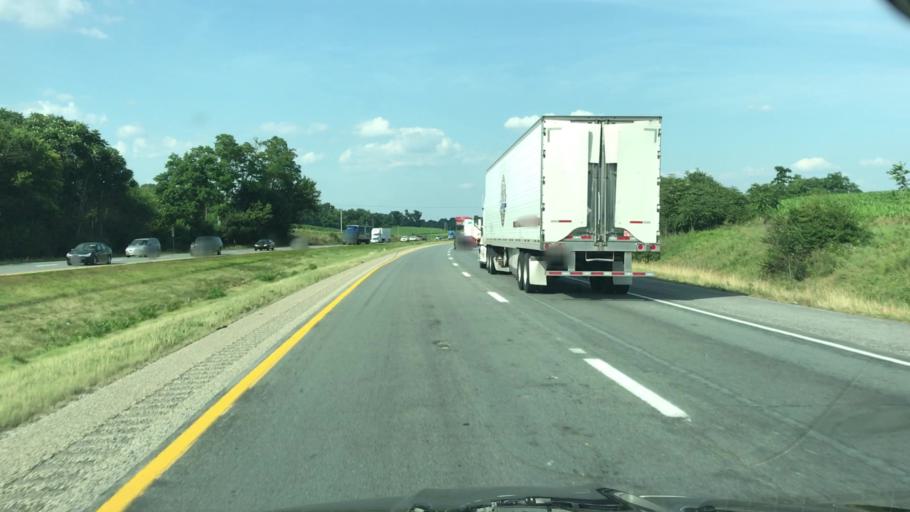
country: US
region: Pennsylvania
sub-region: Cumberland County
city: Newville
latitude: 40.1104
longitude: -77.3795
